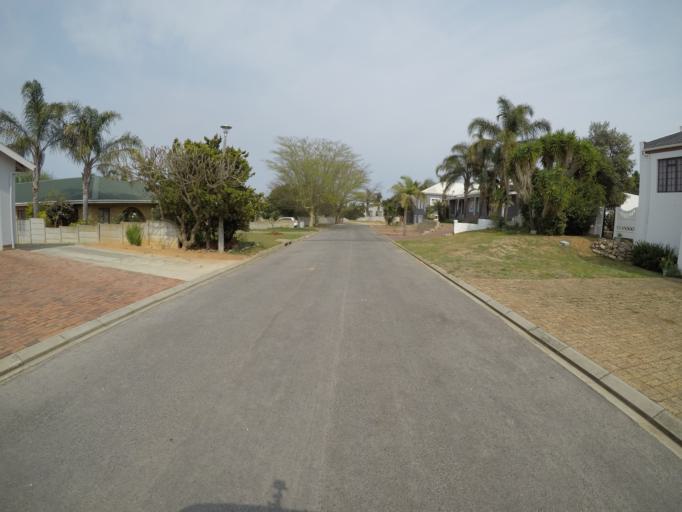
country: ZA
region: Western Cape
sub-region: West Coast District Municipality
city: Malmesbury
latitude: -33.4614
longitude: 18.7407
